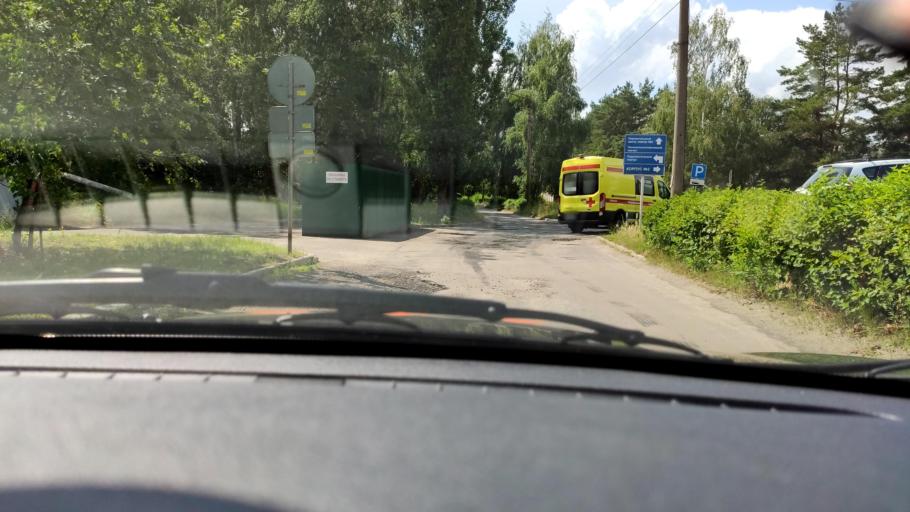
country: RU
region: Voronezj
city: Podgornoye
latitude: 51.7431
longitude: 39.1782
